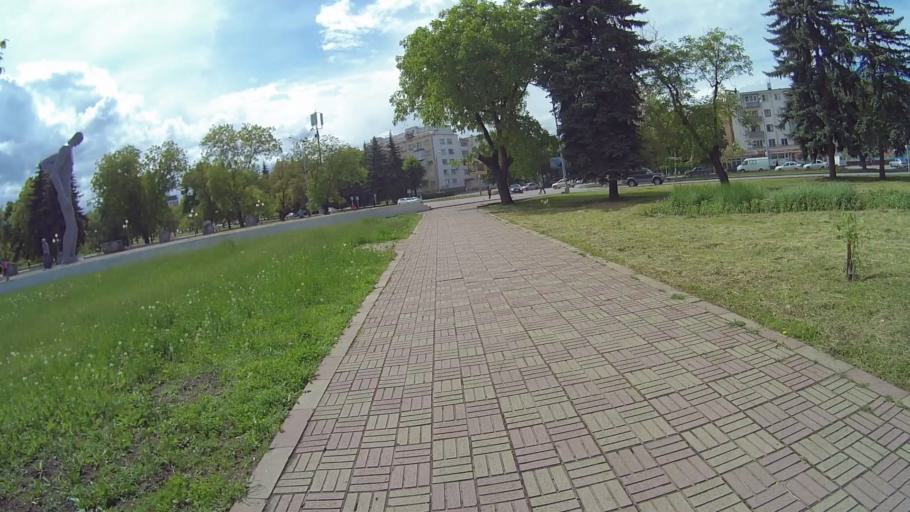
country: RU
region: Kabardino-Balkariya
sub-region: Gorod Nal'chik
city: Nal'chik
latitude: 43.4783
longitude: 43.5877
